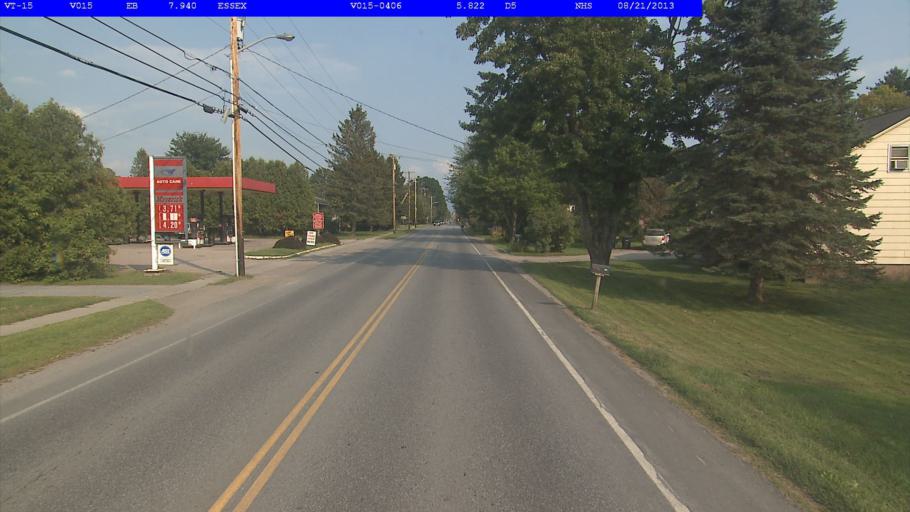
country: US
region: Vermont
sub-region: Chittenden County
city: Jericho
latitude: 44.5081
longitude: -73.0519
